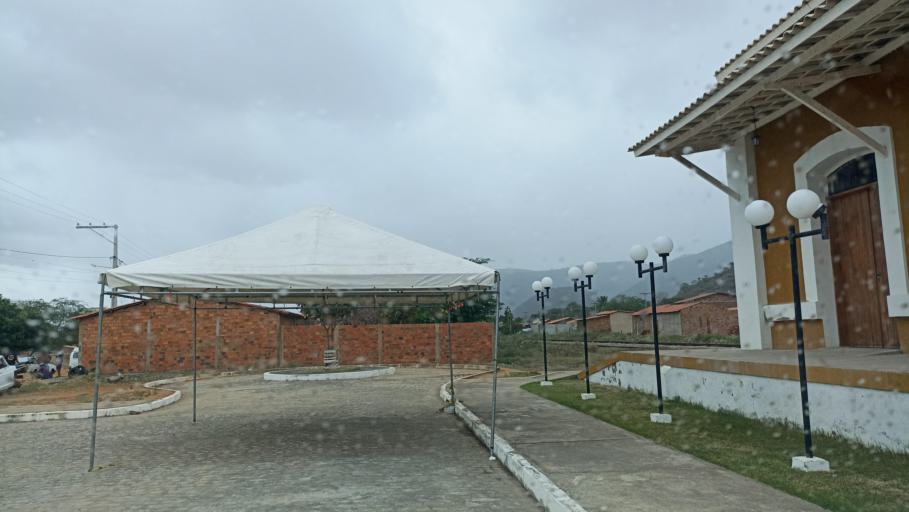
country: BR
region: Bahia
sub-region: Iacu
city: Iacu
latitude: -12.7976
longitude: -40.3510
